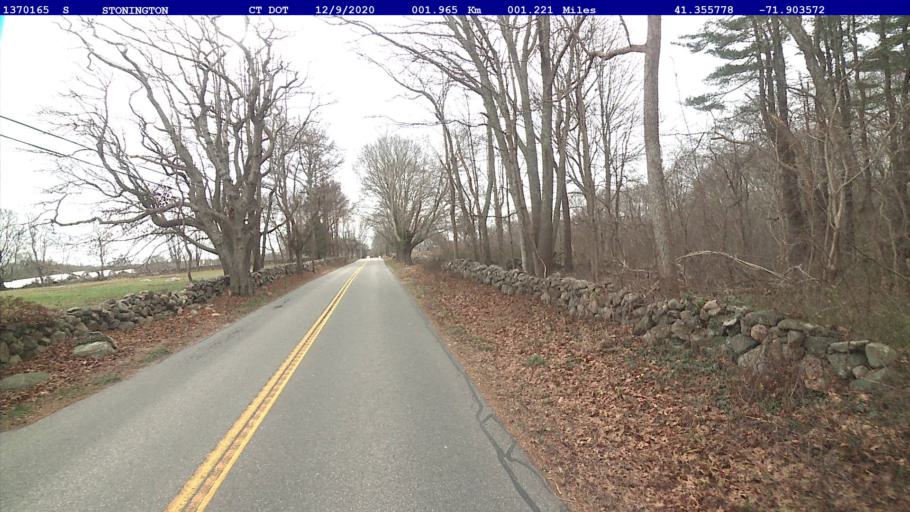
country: US
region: Connecticut
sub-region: New London County
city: Mystic
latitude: 41.3558
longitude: -71.9036
